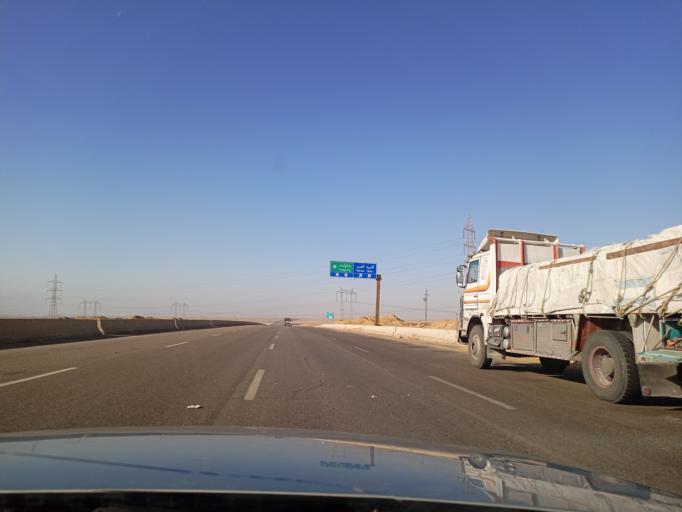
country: EG
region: Muhafazat al Fayyum
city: Tamiyah
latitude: 29.6316
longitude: 30.9724
